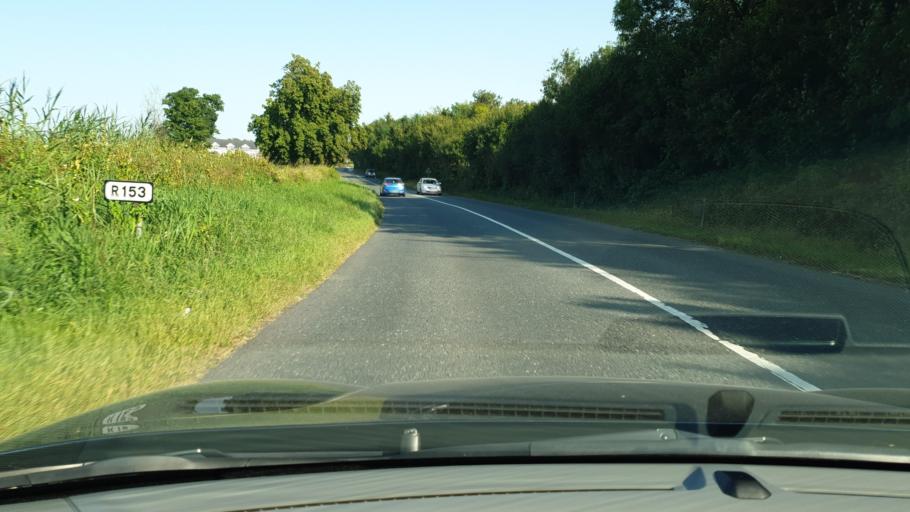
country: IE
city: Kentstown
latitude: 53.6230
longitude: -6.5177
